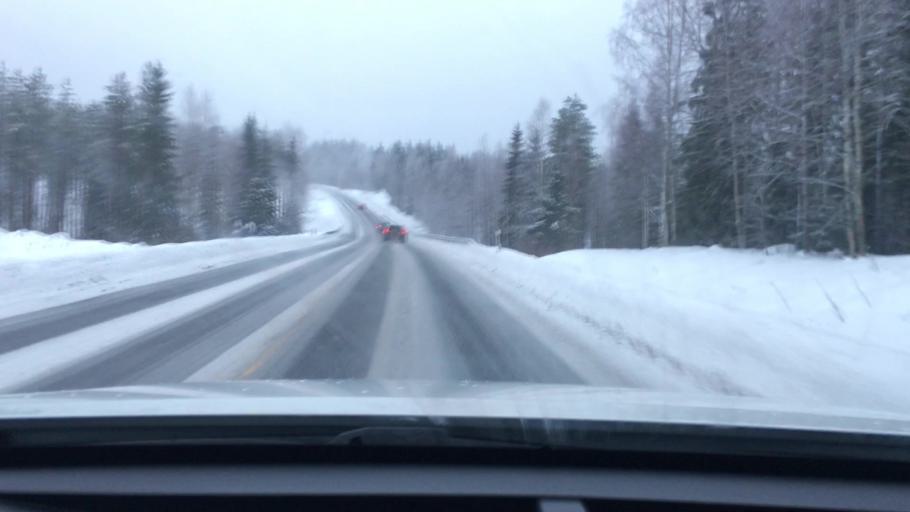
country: FI
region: Northern Savo
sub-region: Ylae-Savo
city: Sonkajaervi
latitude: 63.7578
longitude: 27.3954
